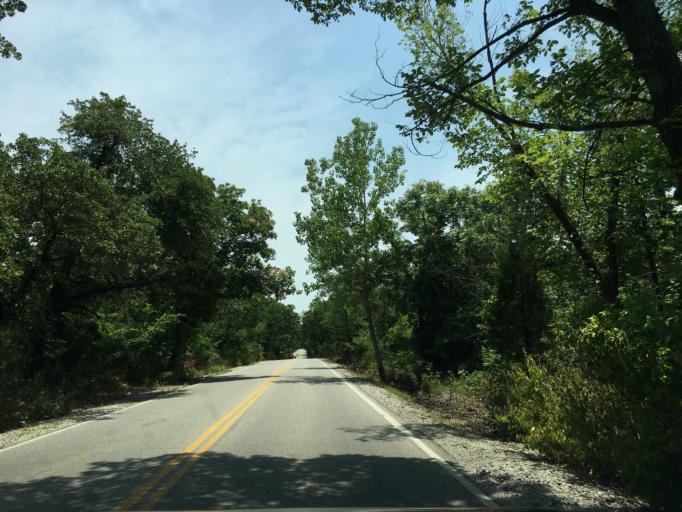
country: US
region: Oklahoma
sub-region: Tulsa County
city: Jenks
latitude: 36.0746
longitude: -95.9994
